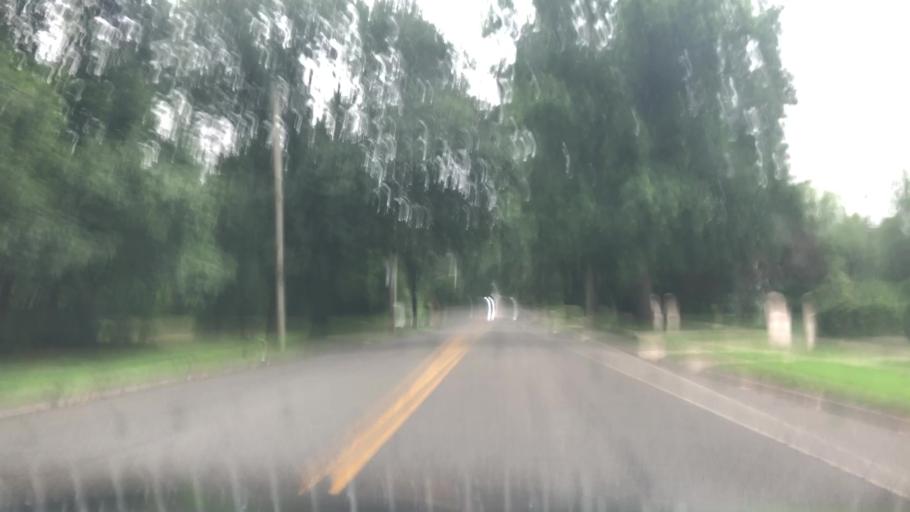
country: US
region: New York
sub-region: Nassau County
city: Garden City
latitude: 40.7118
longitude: -73.6363
